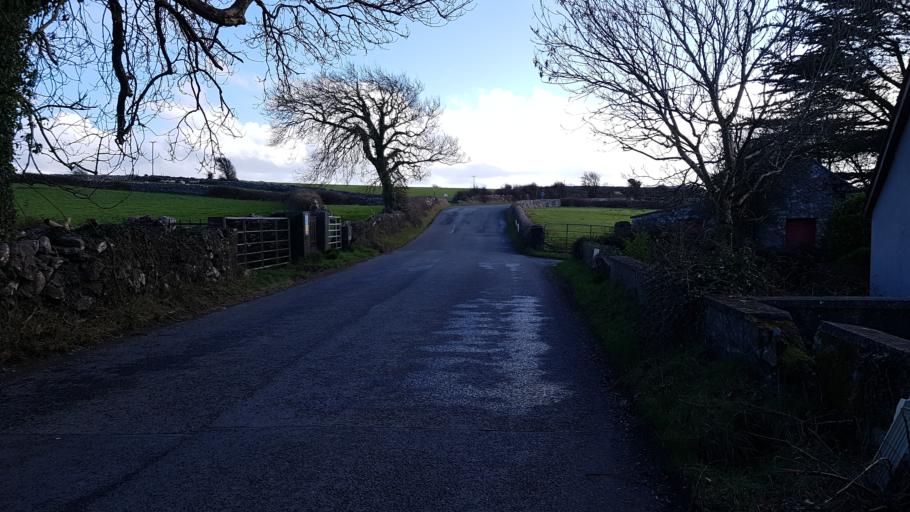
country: IE
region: Connaught
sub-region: County Galway
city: Gaillimh
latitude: 53.3079
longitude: -9.0200
